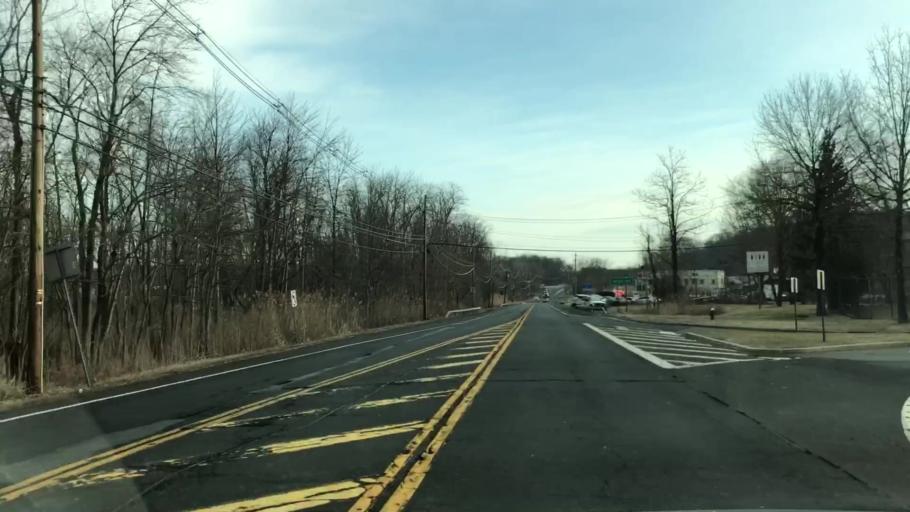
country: US
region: New York
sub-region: Rockland County
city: Mount Ivy
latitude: 41.1837
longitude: -74.0468
